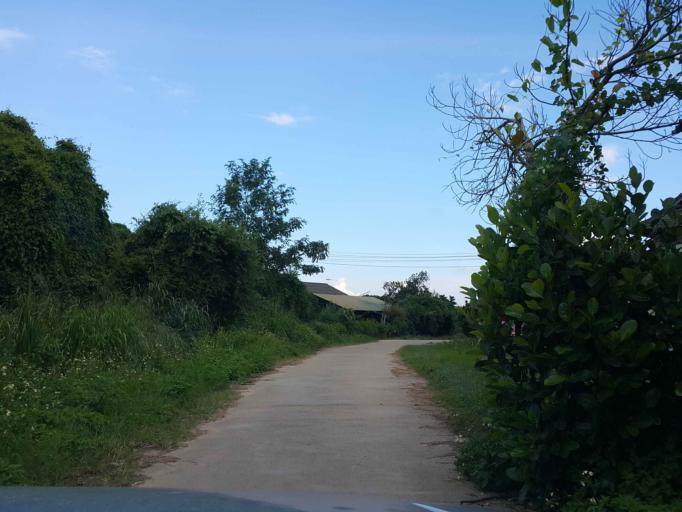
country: TH
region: Chiang Mai
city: Mae Taeng
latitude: 18.9976
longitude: 98.9479
